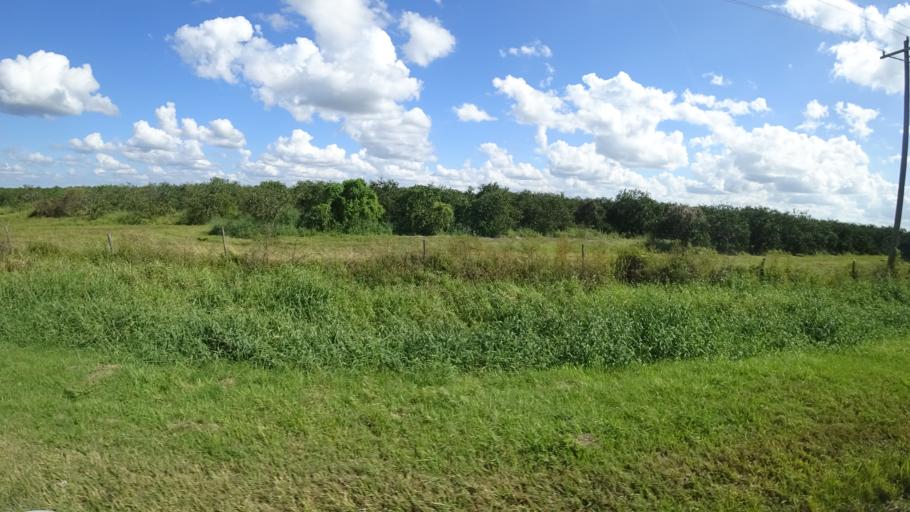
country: US
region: Florida
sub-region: Sarasota County
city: Lake Sarasota
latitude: 27.3953
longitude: -82.1328
